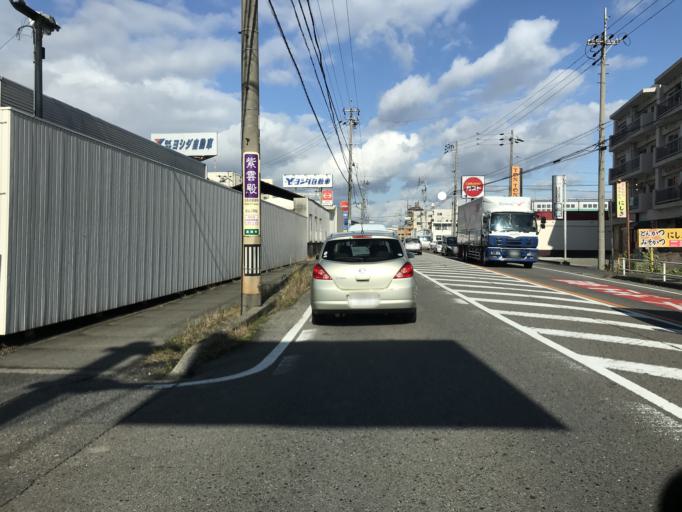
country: JP
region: Aichi
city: Komaki
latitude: 35.2421
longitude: 136.8957
